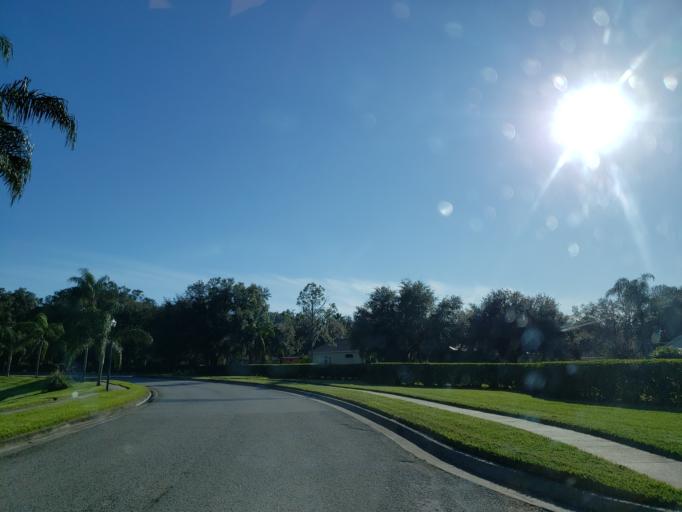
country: US
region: Florida
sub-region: Hillsborough County
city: Bloomingdale
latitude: 27.9016
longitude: -82.2118
